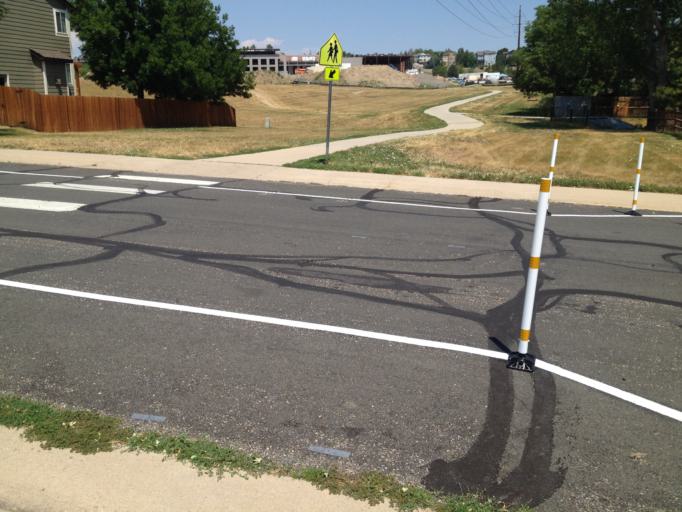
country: US
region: Colorado
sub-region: Boulder County
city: Superior
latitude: 39.9719
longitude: -105.1561
